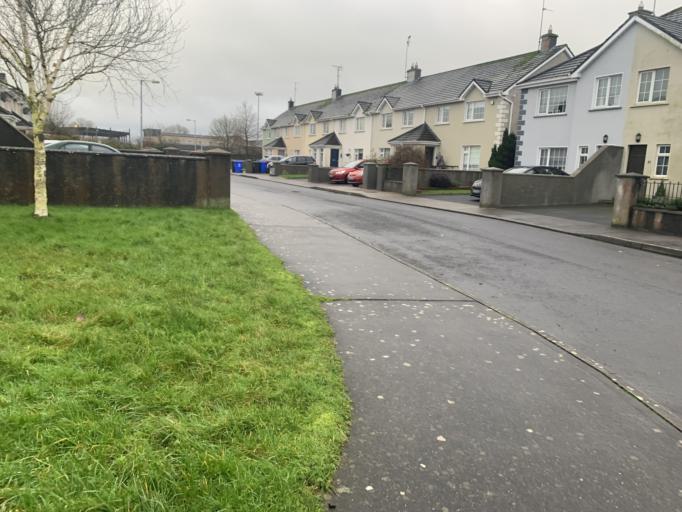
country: IE
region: Connaught
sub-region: County Galway
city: Tuam
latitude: 53.5274
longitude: -8.8552
